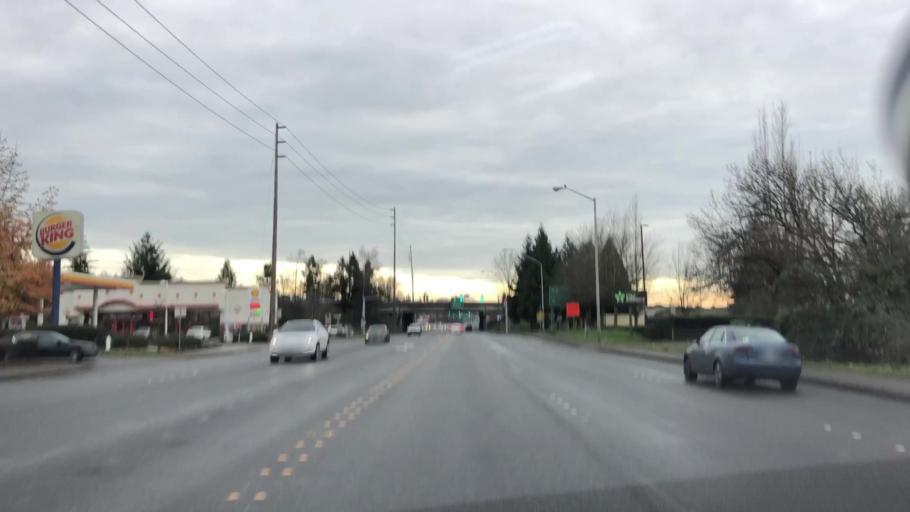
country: US
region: Washington
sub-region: King County
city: Kent
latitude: 47.4006
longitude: -122.2281
